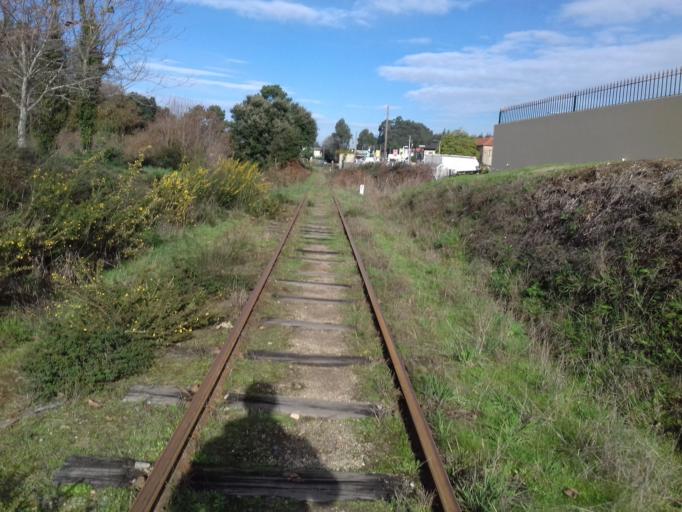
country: PT
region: Aveiro
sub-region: Albergaria-A-Velha
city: Branca
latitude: 40.7670
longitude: -8.4830
